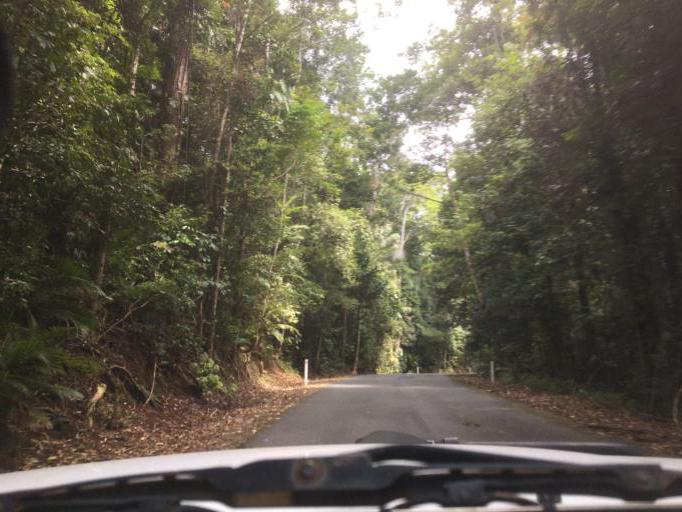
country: AU
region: Queensland
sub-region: Tablelands
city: Tolga
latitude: -17.2819
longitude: 145.6201
